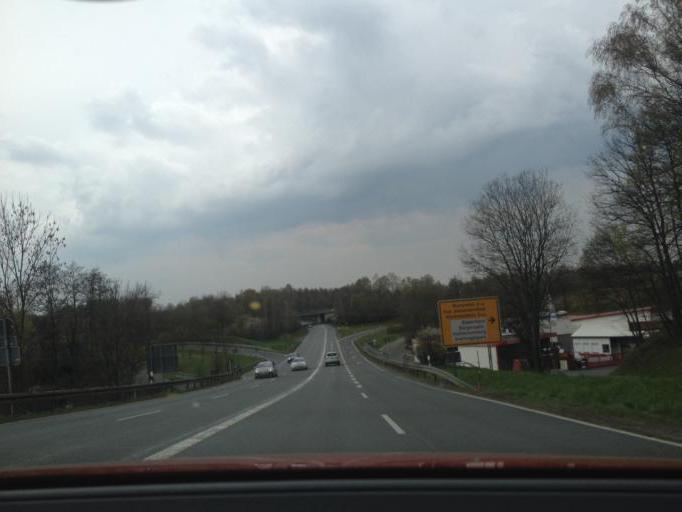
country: DE
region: Bavaria
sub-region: Upper Franconia
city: Bad Alexandersbad
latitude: 50.0209
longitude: 12.0229
